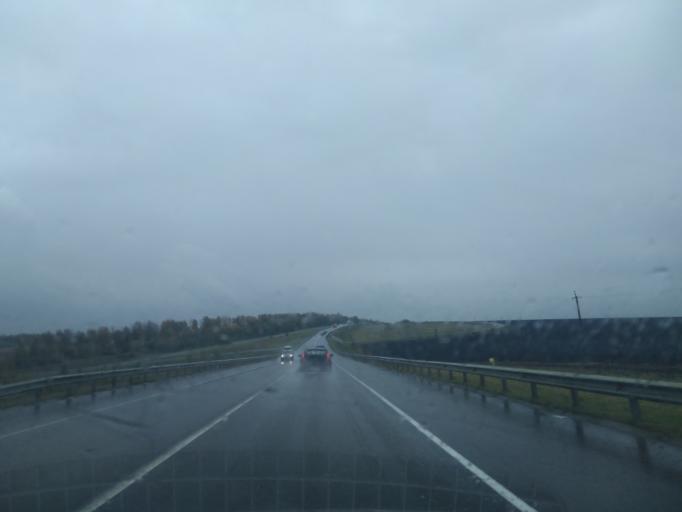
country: RU
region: Tula
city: Shchekino
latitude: 53.9508
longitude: 37.4866
